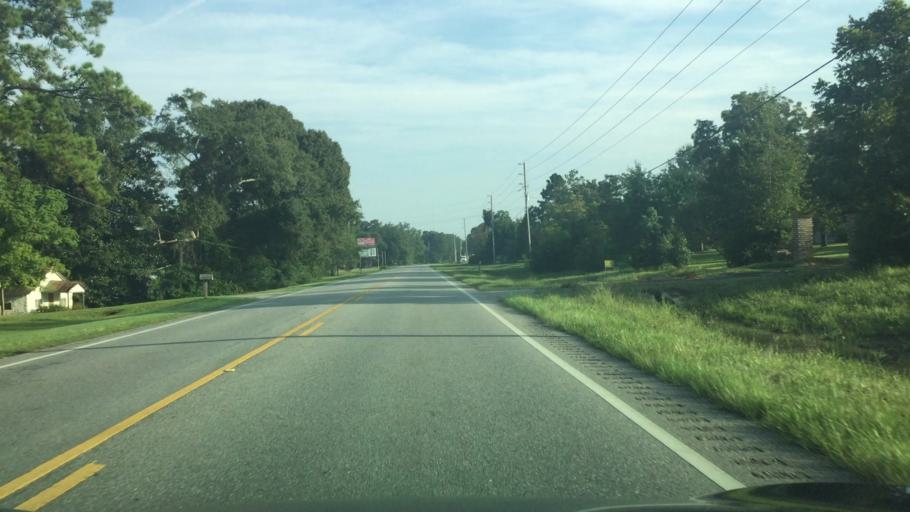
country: US
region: Alabama
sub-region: Covington County
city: Andalusia
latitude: 31.2660
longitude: -86.4727
